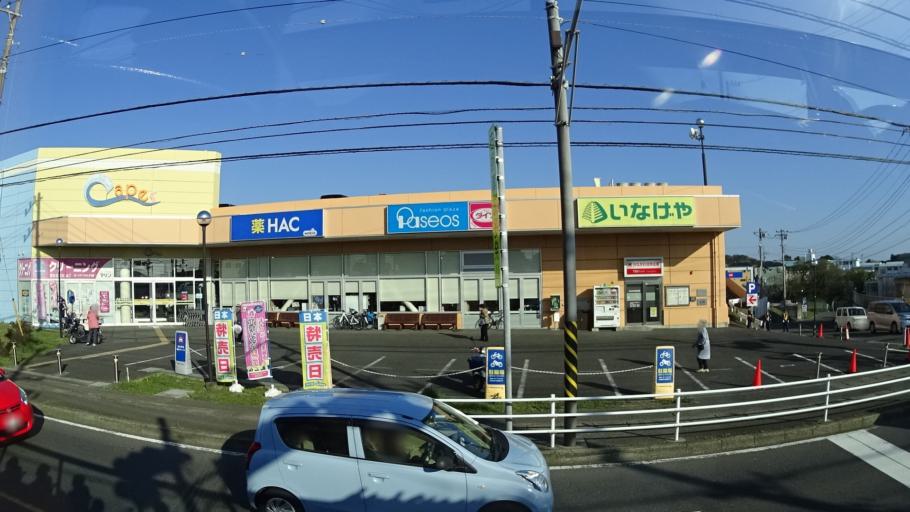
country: JP
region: Kanagawa
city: Miura
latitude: 35.1583
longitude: 139.6384
